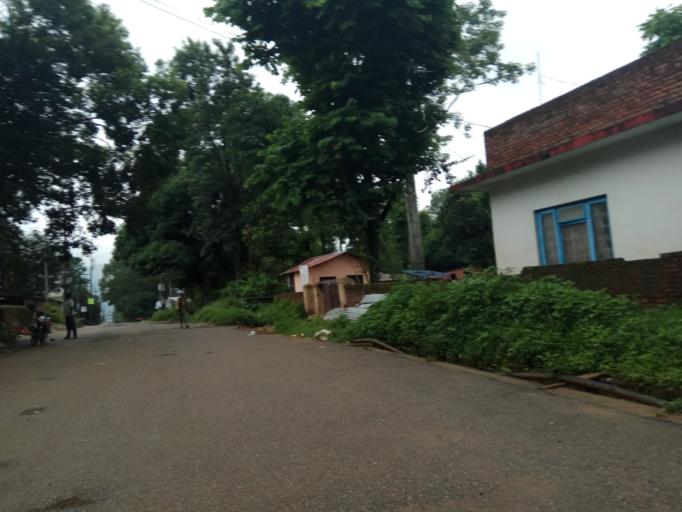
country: NP
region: Central Region
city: Kirtipur
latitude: 27.9101
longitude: 84.8991
